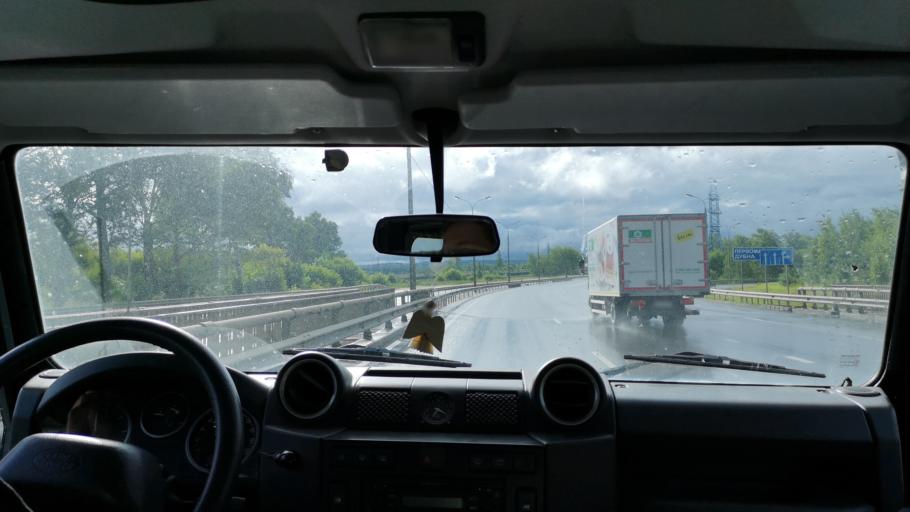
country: RU
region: Moskovskaya
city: Dmitrov
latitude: 56.3651
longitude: 37.4745
